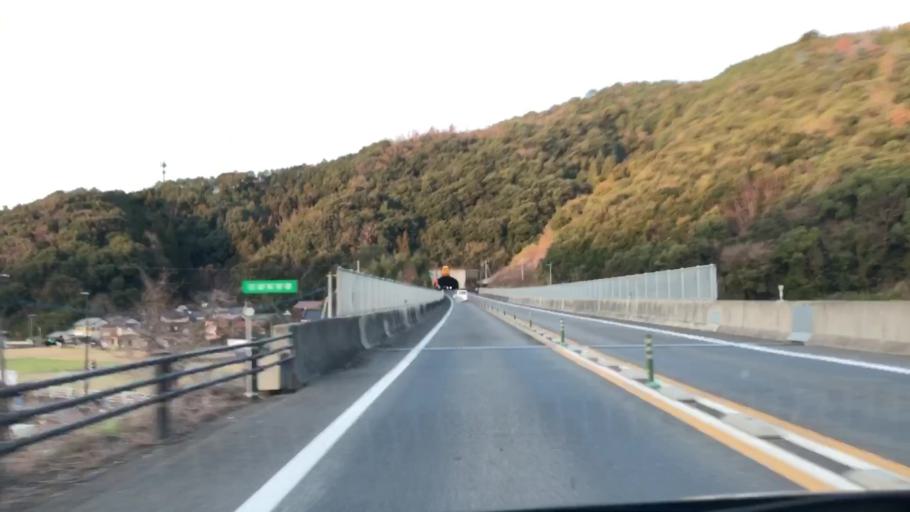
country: JP
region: Kumamoto
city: Minamata
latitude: 32.3010
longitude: 130.5102
